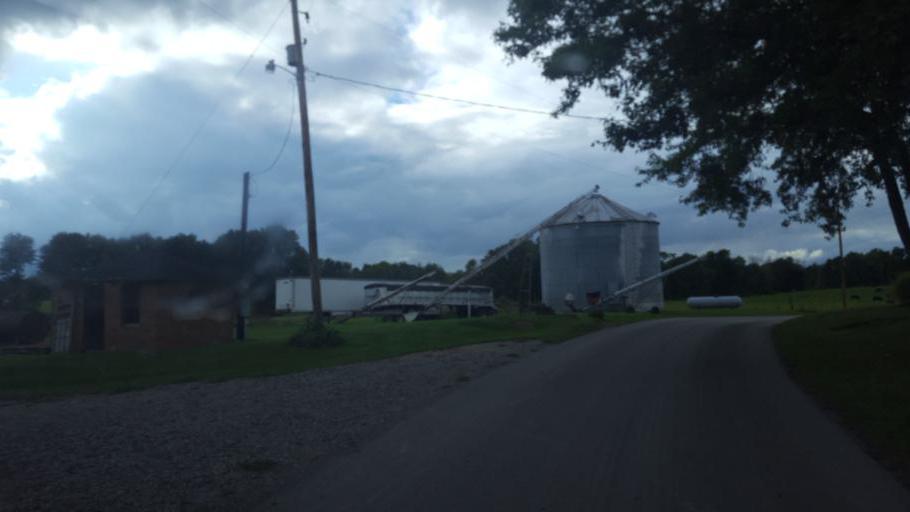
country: US
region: Ohio
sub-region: Jackson County
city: Oak Hill
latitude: 38.9406
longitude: -82.6279
